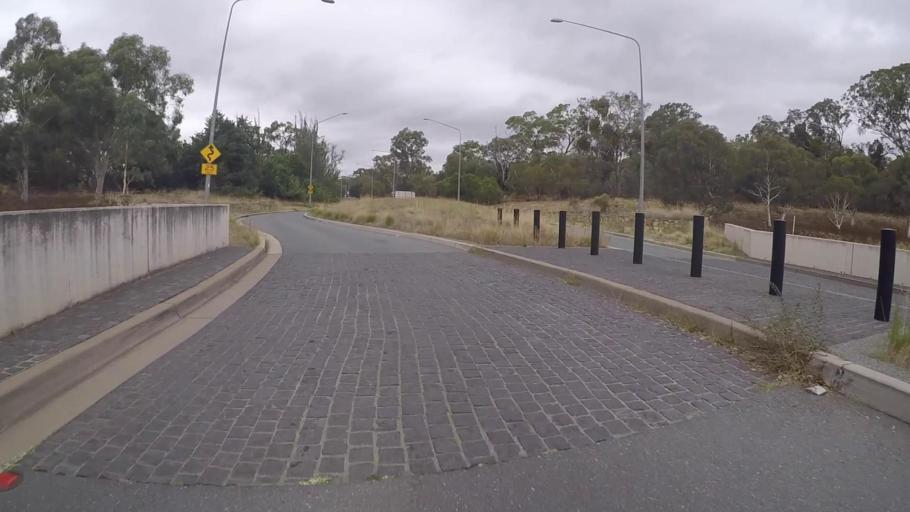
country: AU
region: Australian Capital Territory
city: Canberra
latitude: -35.2966
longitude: 149.1540
